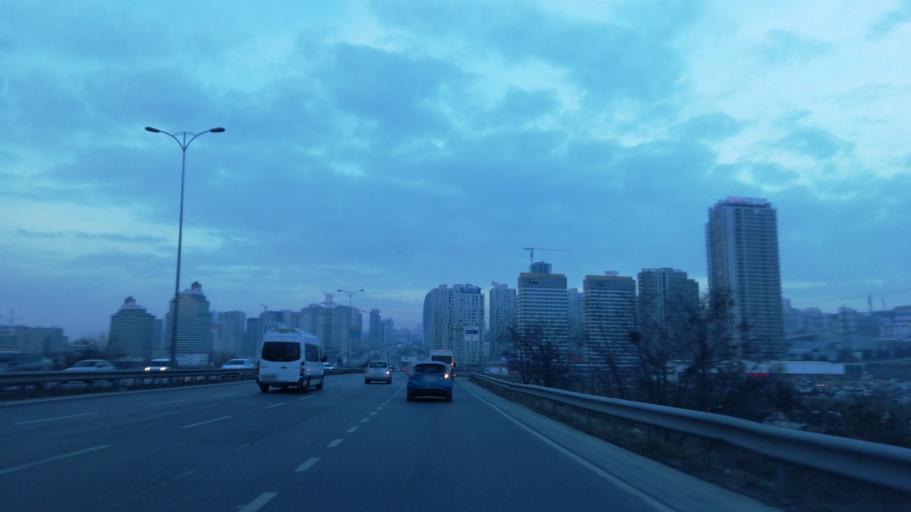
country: TR
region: Istanbul
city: Yakuplu
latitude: 41.0029
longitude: 28.6775
